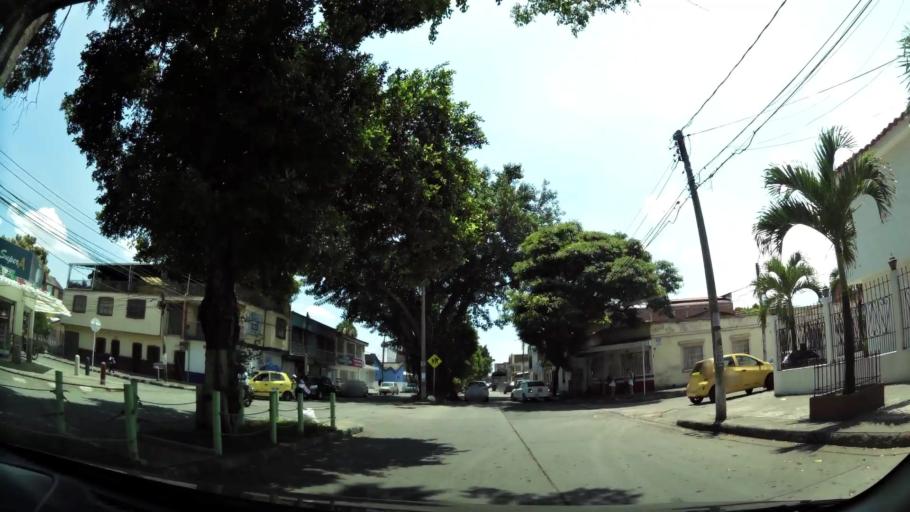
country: CO
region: Valle del Cauca
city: Cali
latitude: 3.4500
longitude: -76.4989
